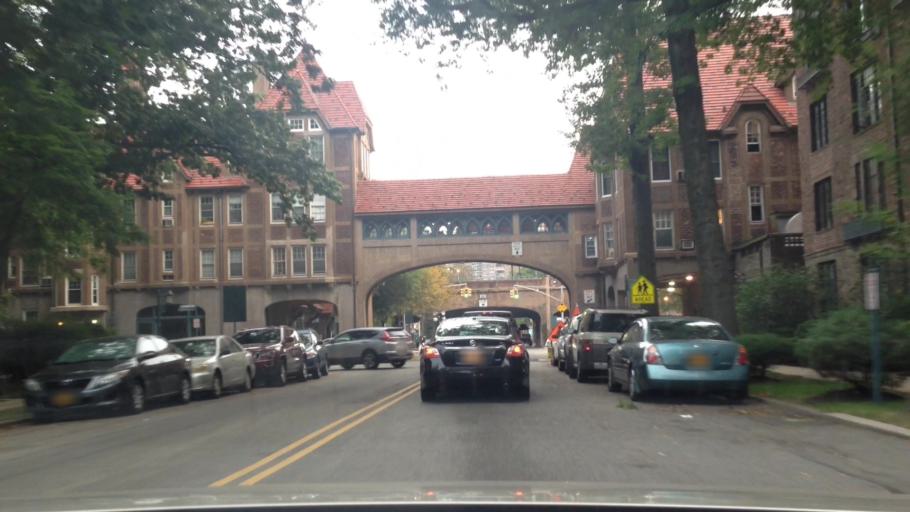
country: US
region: New York
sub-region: Queens County
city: Borough of Queens
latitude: 40.7187
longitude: -73.8458
